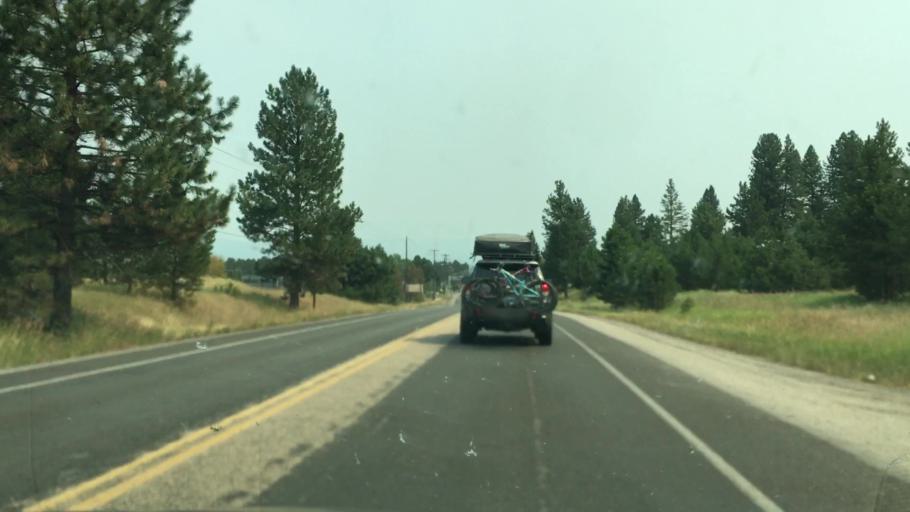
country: US
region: Idaho
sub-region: Valley County
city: Cascade
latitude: 44.5089
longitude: -116.0345
